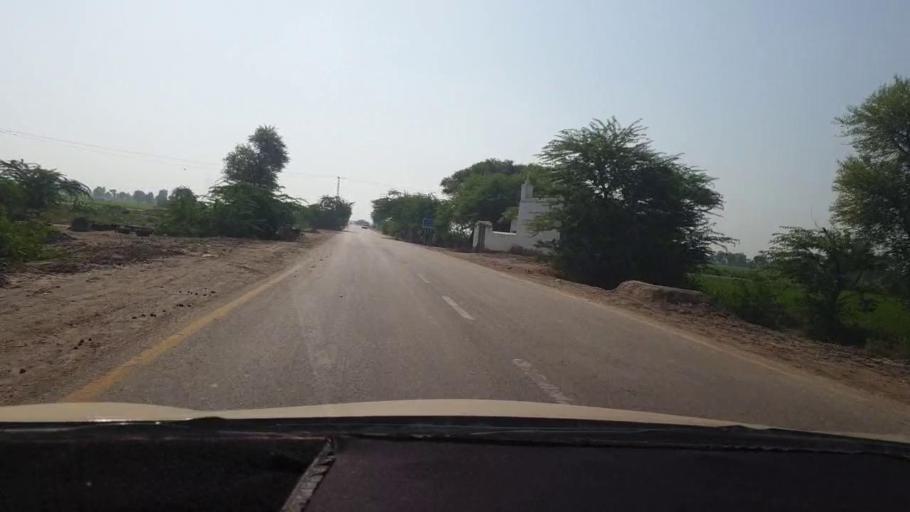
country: PK
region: Sindh
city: Miro Khan
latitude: 27.7218
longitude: 68.1424
